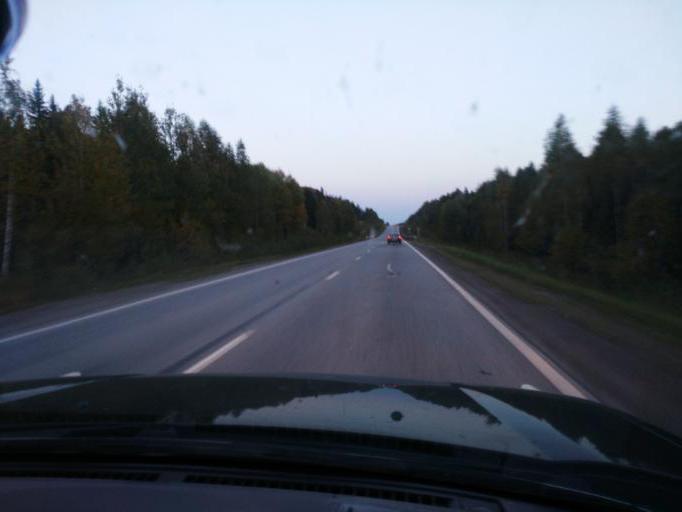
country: RU
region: Perm
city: Verkhnechusovskiye Gorodki
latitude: 58.2731
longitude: 56.9434
